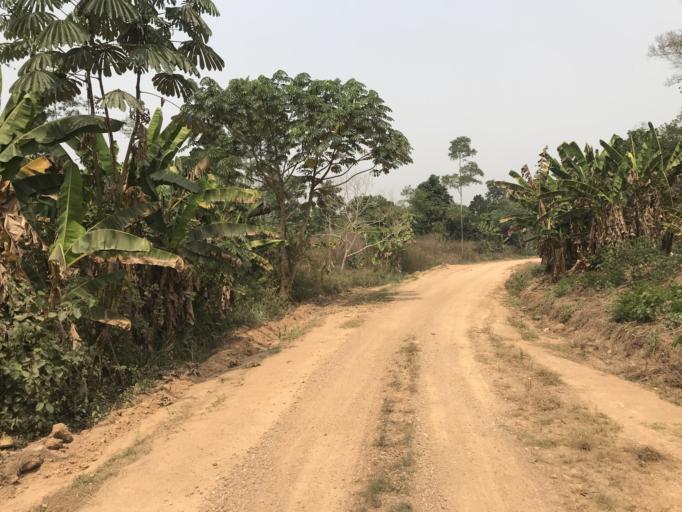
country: NG
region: Osun
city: Ifetedo
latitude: 7.0366
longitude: 4.4536
